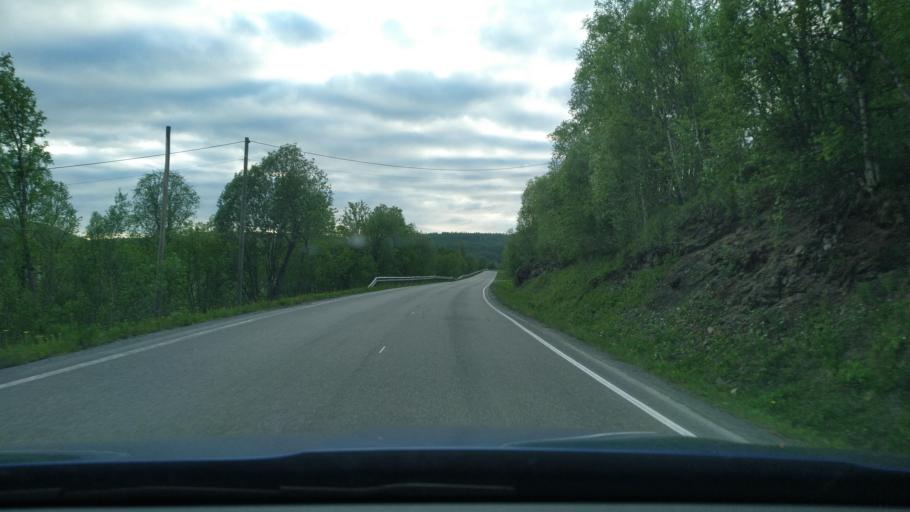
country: NO
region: Troms
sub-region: Sorreisa
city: Sorreisa
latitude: 69.0896
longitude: 18.3485
